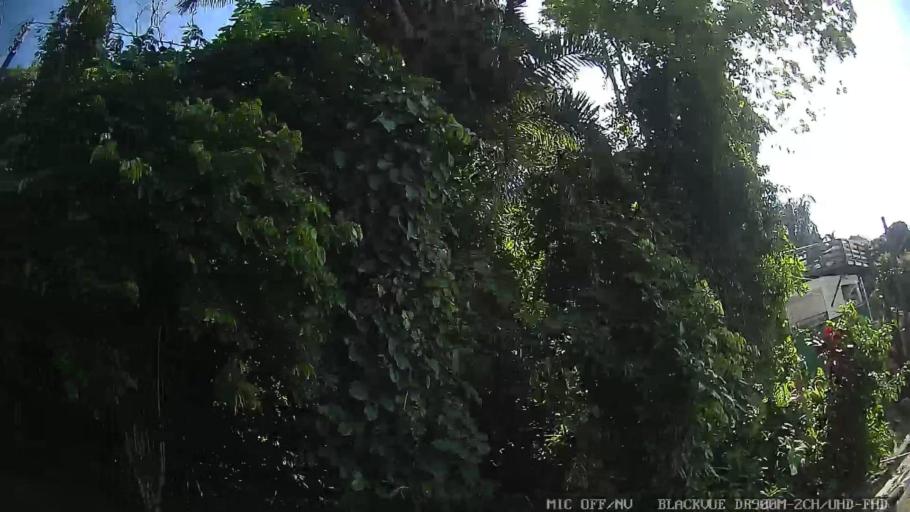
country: BR
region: Sao Paulo
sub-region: Guaruja
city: Guaruja
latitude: -23.9869
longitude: -46.1888
